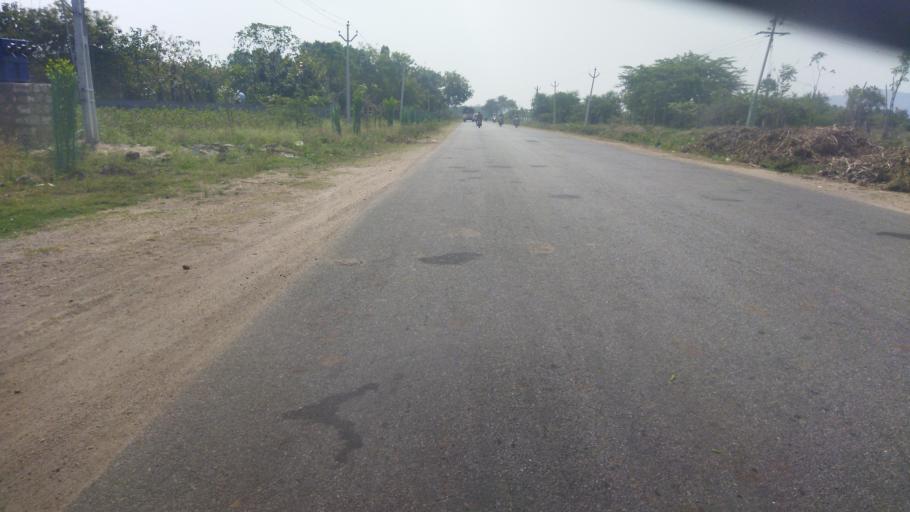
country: IN
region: Telangana
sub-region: Nalgonda
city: Nalgonda
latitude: 17.0961
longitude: 79.2858
